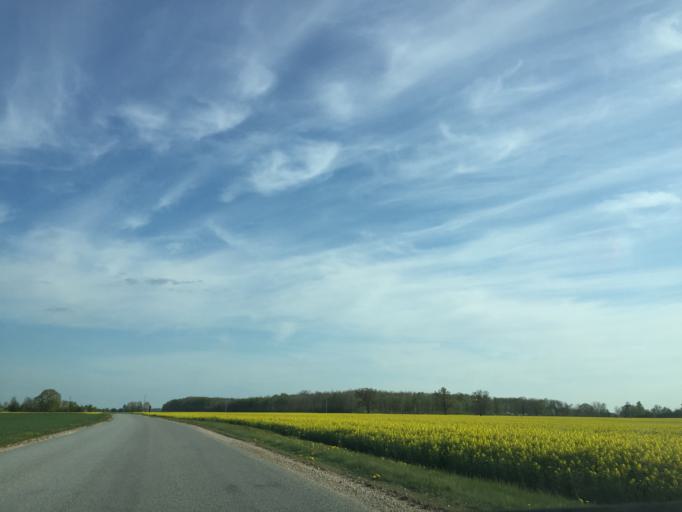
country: LV
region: Bauskas Rajons
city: Bauska
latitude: 56.3871
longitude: 24.2064
